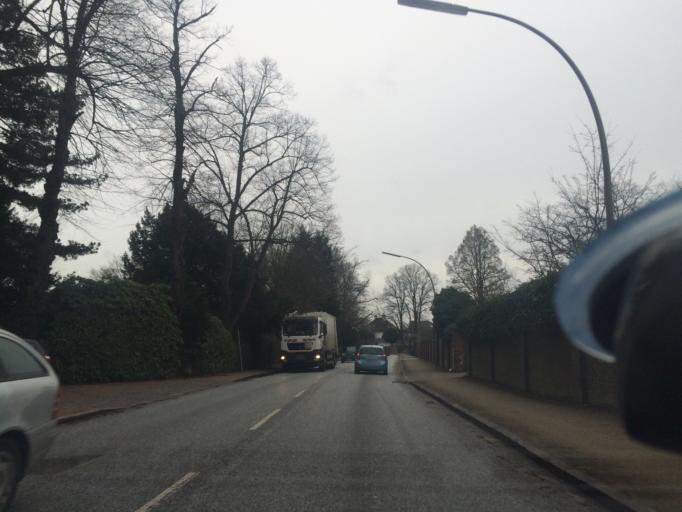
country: DE
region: Schleswig-Holstein
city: Halstenbek
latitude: 53.5526
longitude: 9.8398
